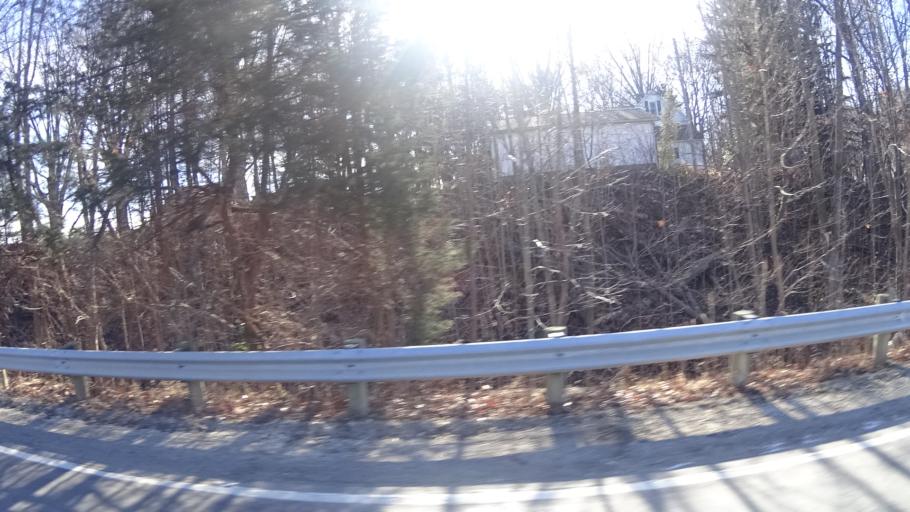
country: US
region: Ohio
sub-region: Lorain County
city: South Amherst
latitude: 41.3531
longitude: -82.3083
